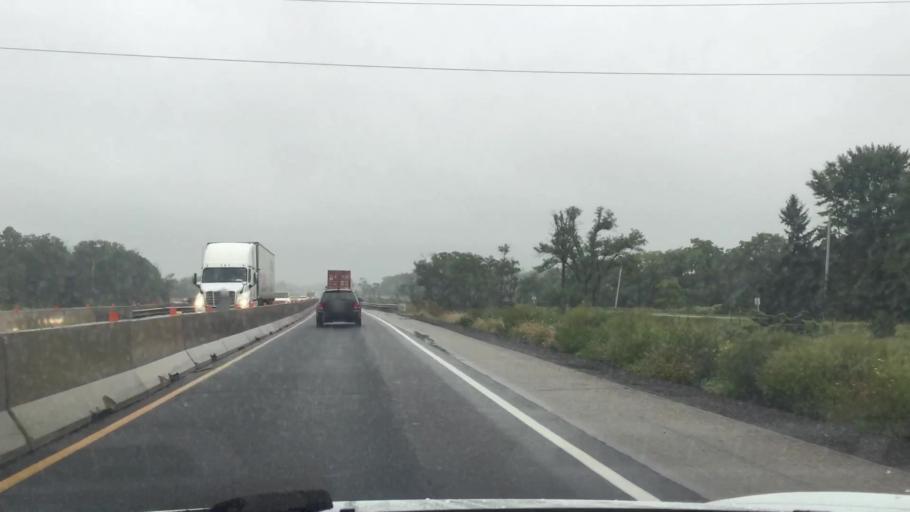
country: CA
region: Ontario
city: St. Thomas
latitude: 42.8167
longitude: -81.3149
